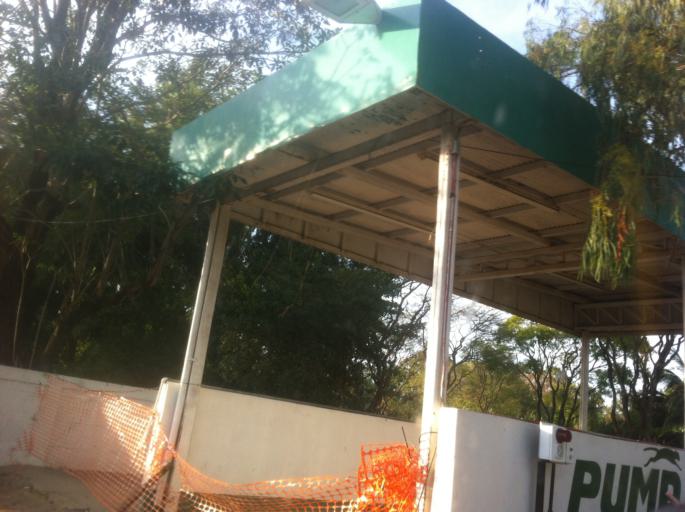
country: NI
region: Rivas
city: Rivas
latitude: 11.4408
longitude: -85.8229
